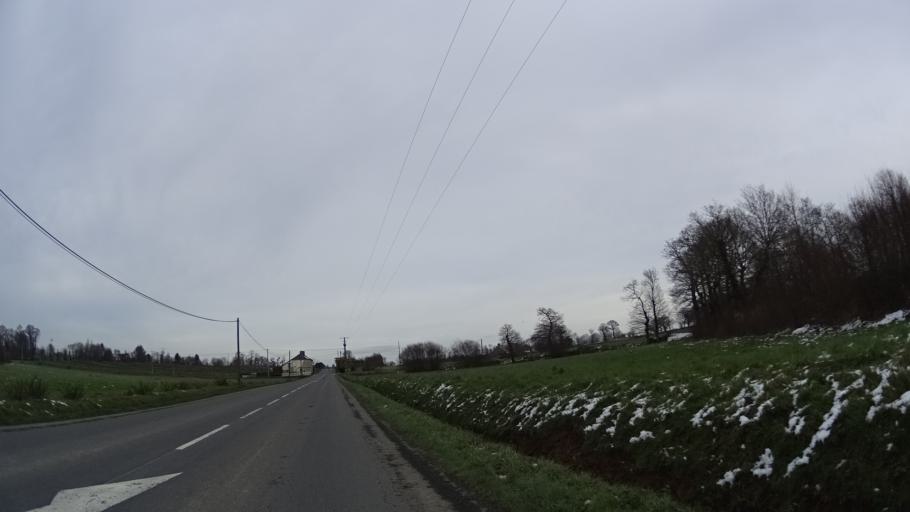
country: FR
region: Brittany
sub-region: Departement d'Ille-et-Vilaine
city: Montauban-de-Bretagne
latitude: 48.2415
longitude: -2.0073
